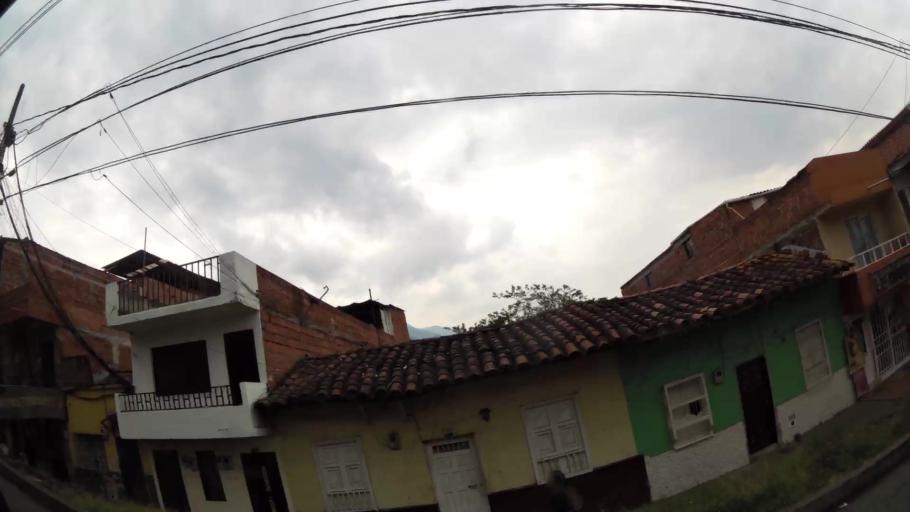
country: CO
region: Antioquia
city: Medellin
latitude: 6.2493
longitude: -75.5504
